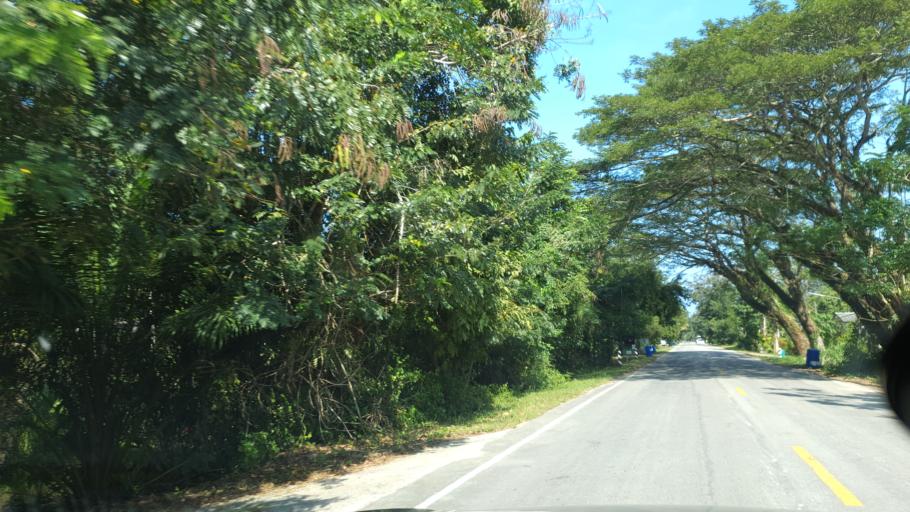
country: TH
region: Surat Thani
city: Tha Chana
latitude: 9.5816
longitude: 99.1938
